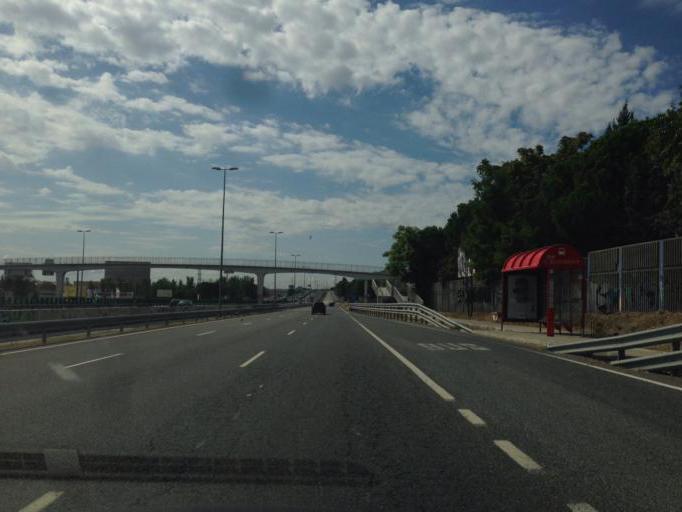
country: ES
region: Madrid
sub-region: Provincia de Madrid
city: San Sebastian de los Reyes
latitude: 40.5897
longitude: -3.5834
